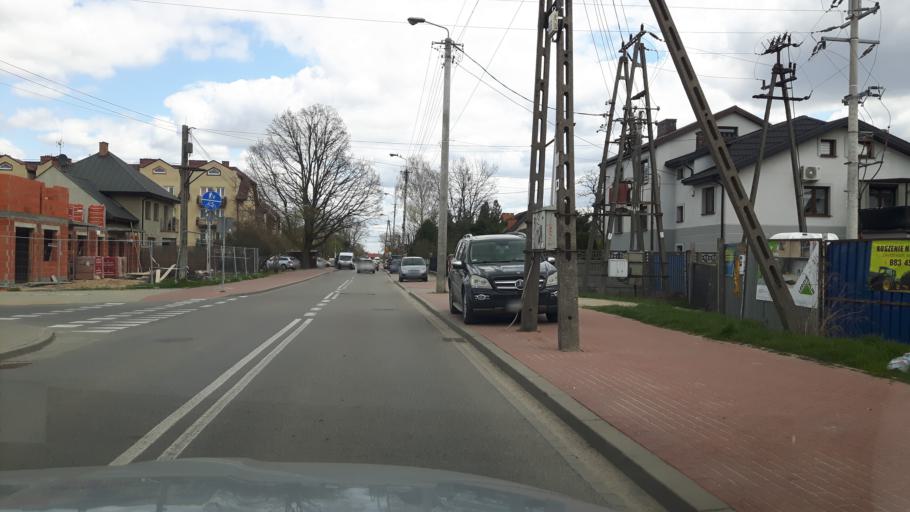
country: PL
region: Masovian Voivodeship
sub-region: Powiat wolominski
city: Wolomin
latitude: 52.3440
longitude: 21.2562
